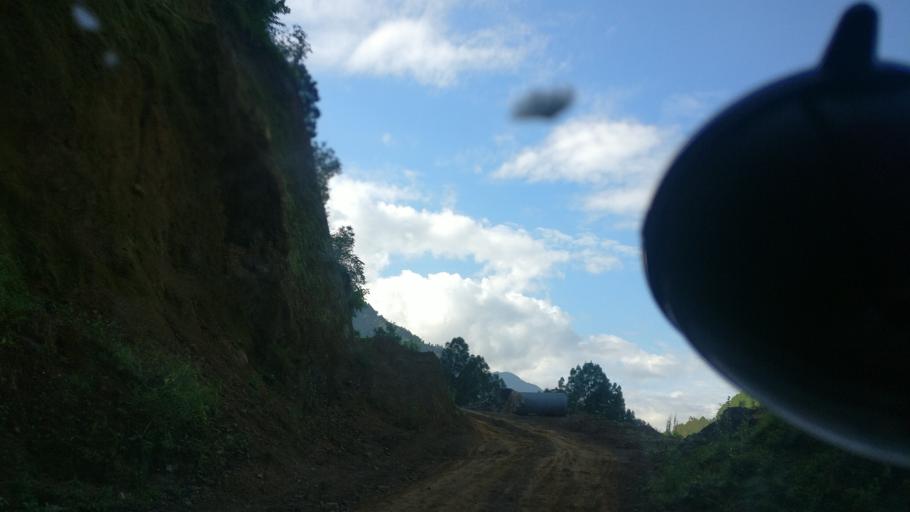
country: NP
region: Western Region
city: Baglung
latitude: 28.1587
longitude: 83.6540
